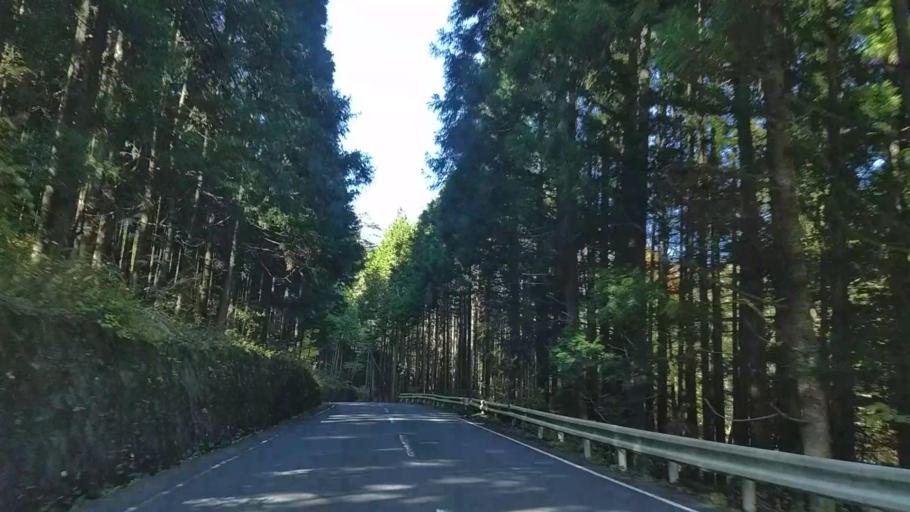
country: JP
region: Yamanashi
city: Otsuki
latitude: 35.7408
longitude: 138.9676
